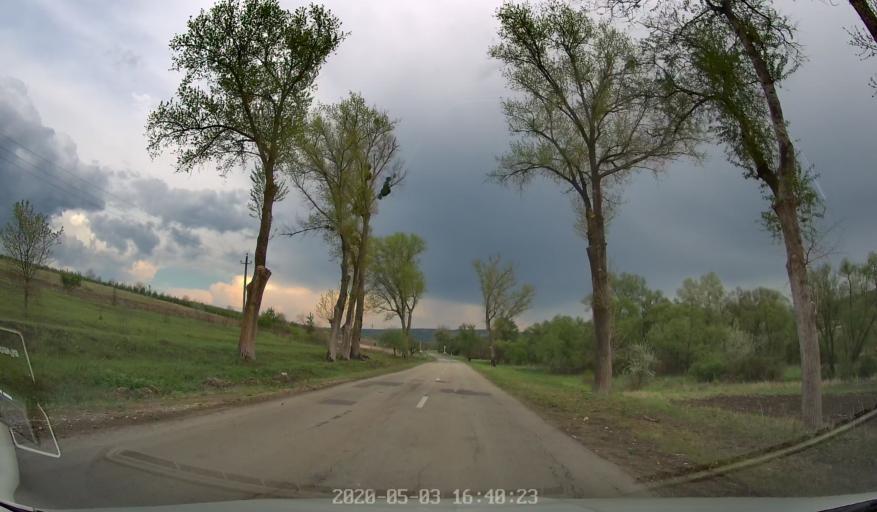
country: MD
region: Stinga Nistrului
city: Bucovat
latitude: 47.1751
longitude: 28.3911
